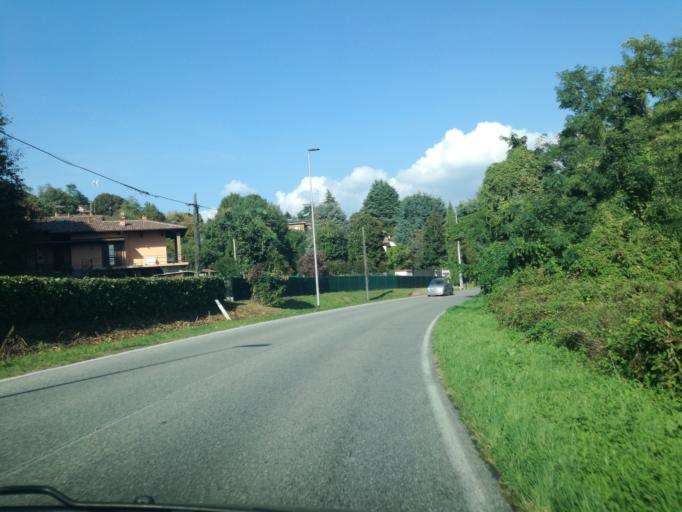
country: IT
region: Lombardy
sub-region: Provincia di Lecco
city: Brivio
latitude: 45.7349
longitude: 9.4439
